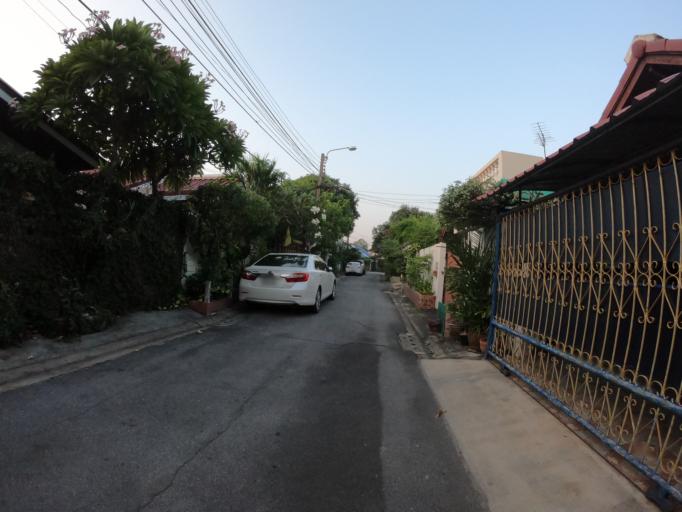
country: TH
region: Bangkok
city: Lat Phrao
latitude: 13.8285
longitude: 100.6192
